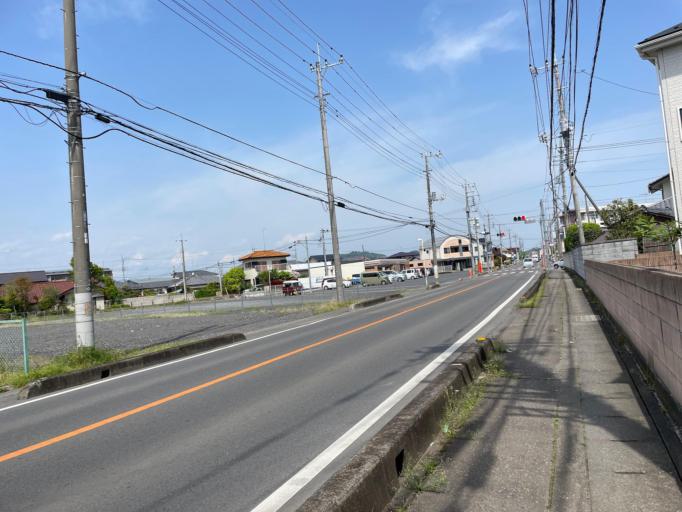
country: JP
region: Gunma
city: Ota
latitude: 36.2907
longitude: 139.3445
